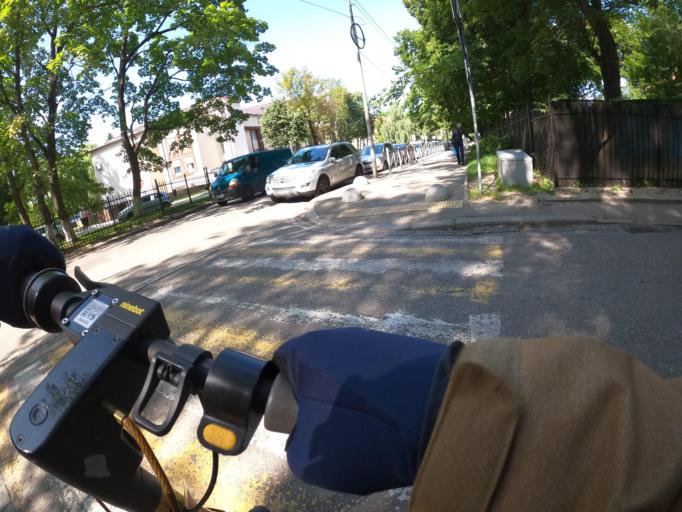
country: RU
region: Kaliningrad
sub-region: Gorod Kaliningrad
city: Kaliningrad
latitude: 54.7230
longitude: 20.5104
